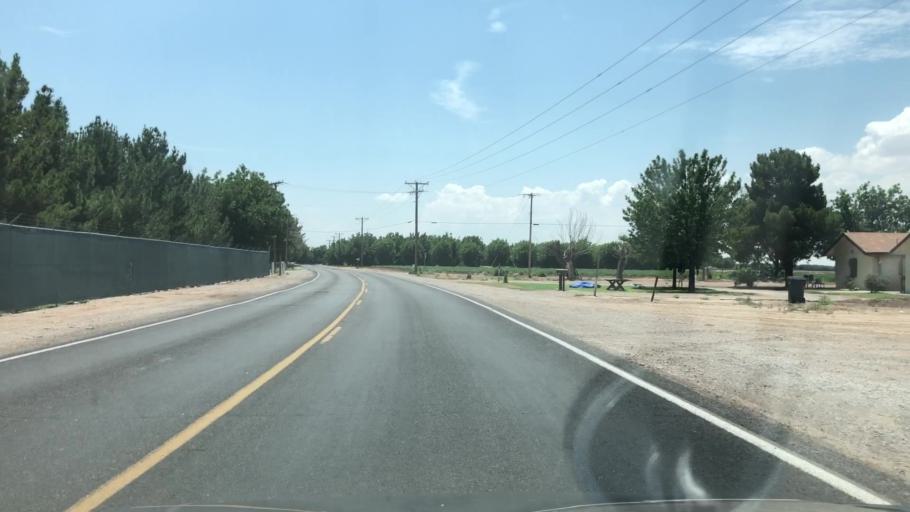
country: US
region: New Mexico
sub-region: Dona Ana County
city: La Union
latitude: 31.9530
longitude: -106.6443
